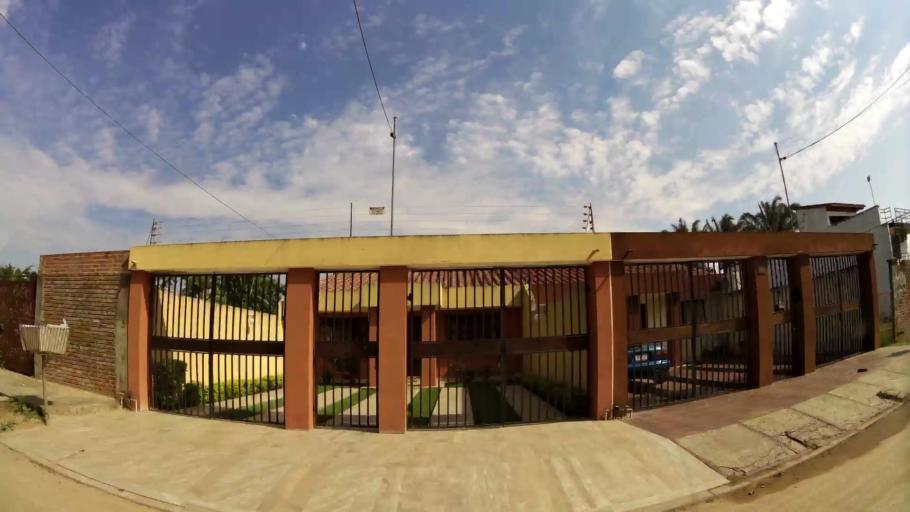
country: BO
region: Santa Cruz
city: Santa Cruz de la Sierra
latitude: -17.7257
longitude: -63.1530
